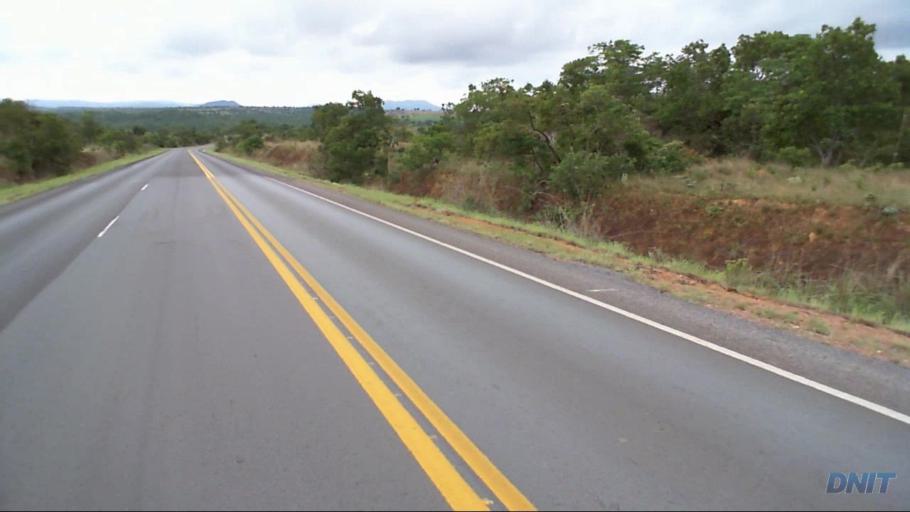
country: BR
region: Goias
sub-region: Padre Bernardo
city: Padre Bernardo
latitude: -15.2109
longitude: -48.5696
